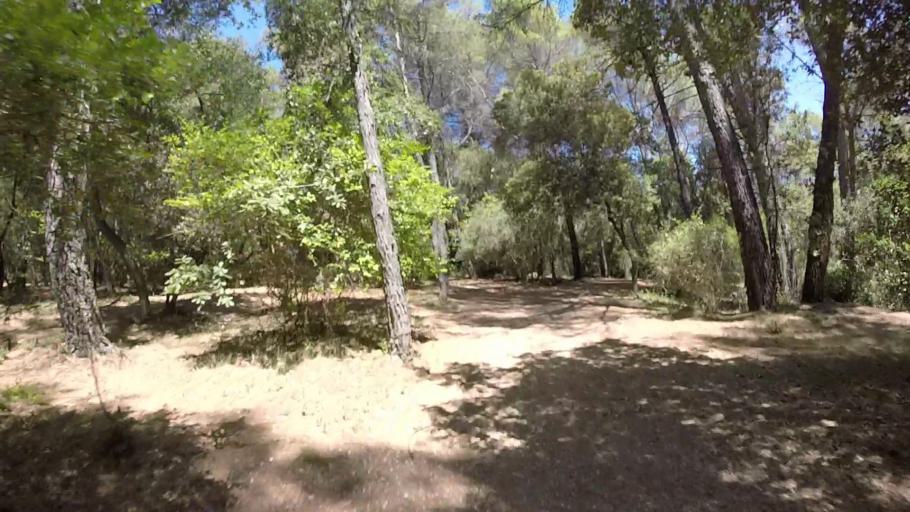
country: FR
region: Provence-Alpes-Cote d'Azur
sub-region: Departement des Alpes-Maritimes
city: Vallauris
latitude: 43.6069
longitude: 7.0421
